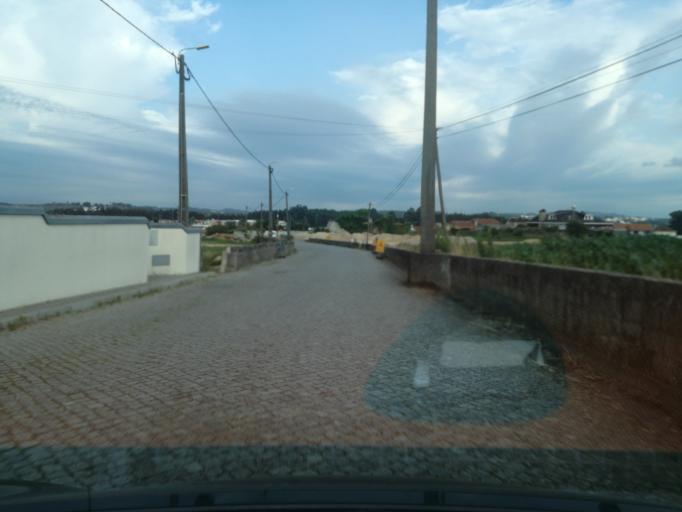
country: PT
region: Porto
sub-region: Maia
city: Anta
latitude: 41.2551
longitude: -8.6105
